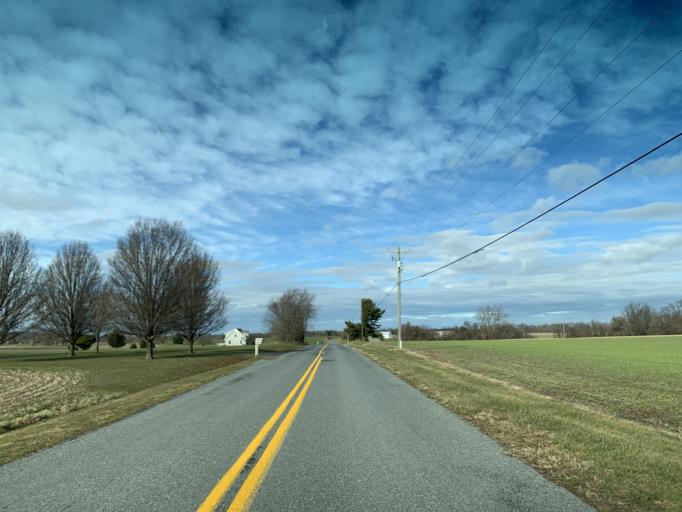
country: US
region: Maryland
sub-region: Kent County
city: Chestertown
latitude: 39.3398
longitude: -76.0496
